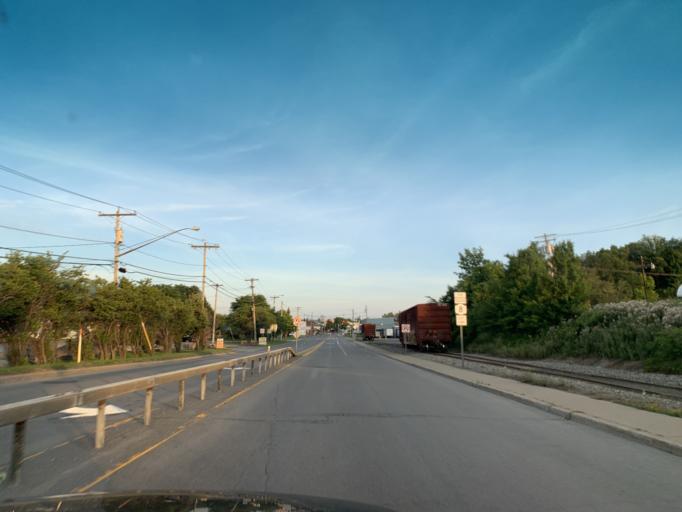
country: US
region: New York
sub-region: Oneida County
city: New Hartford
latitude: 43.0780
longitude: -75.2913
